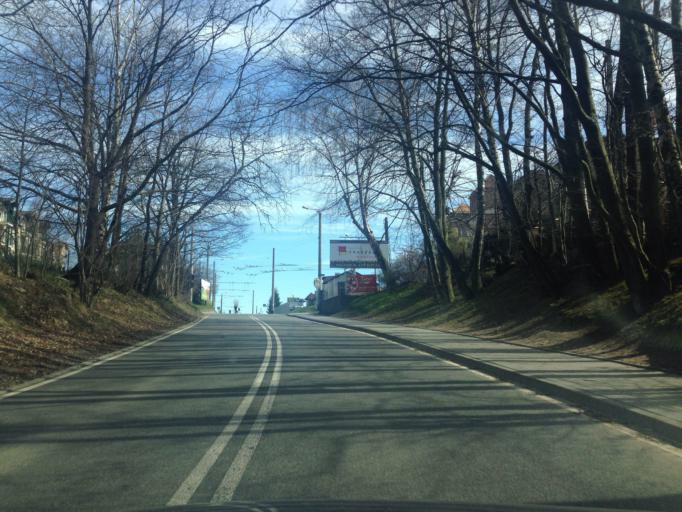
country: PL
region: Pomeranian Voivodeship
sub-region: Gdynia
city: Wielki Kack
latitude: 54.4754
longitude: 18.4618
